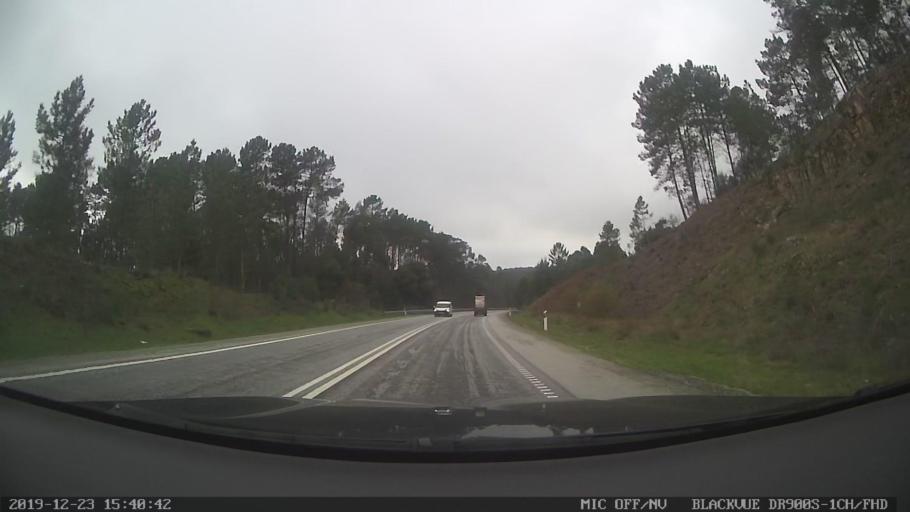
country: PT
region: Viseu
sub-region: Viseu
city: Abraveses
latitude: 40.6754
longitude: -7.9517
